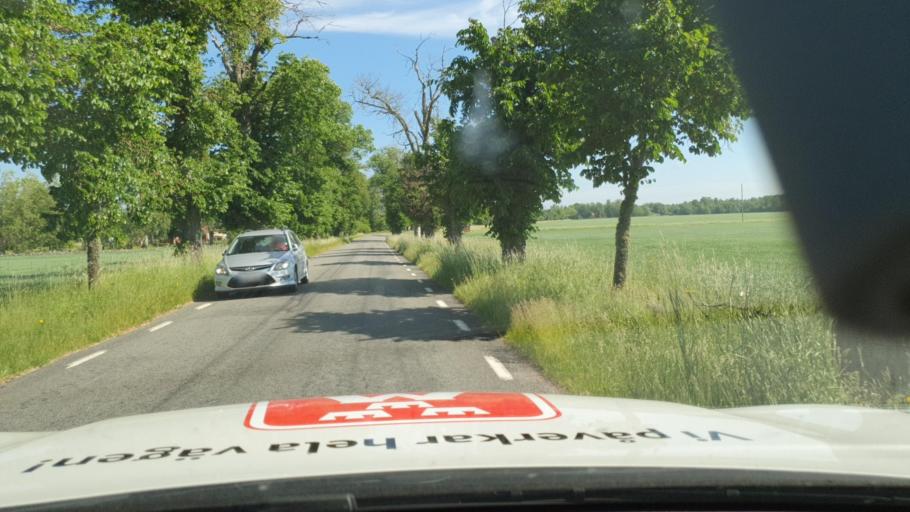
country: SE
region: Vaestra Goetaland
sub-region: Tidaholms Kommun
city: Olofstorp
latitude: 58.2661
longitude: 13.9016
